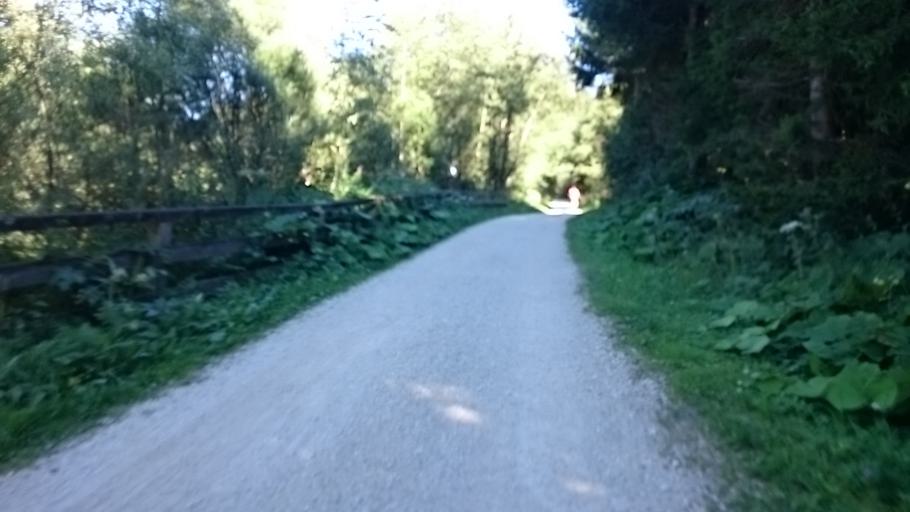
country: IT
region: Trentino-Alto Adige
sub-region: Bolzano
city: Monguelfo
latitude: 46.7601
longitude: 12.0848
